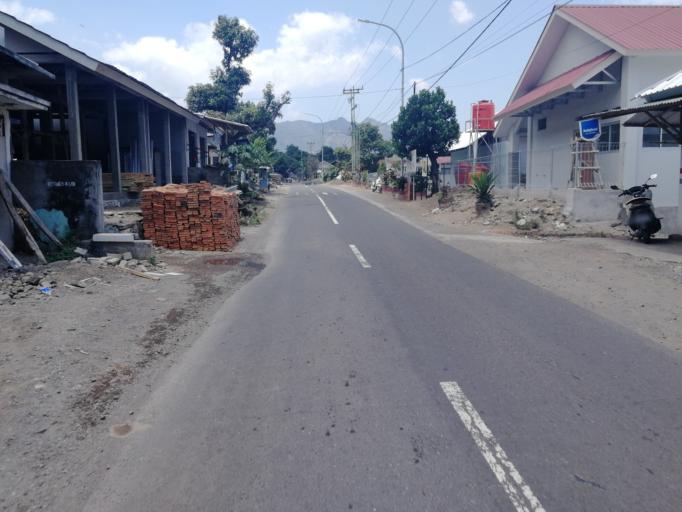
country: ID
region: West Nusa Tenggara
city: Karangsubagan
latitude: -8.4246
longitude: 116.0922
